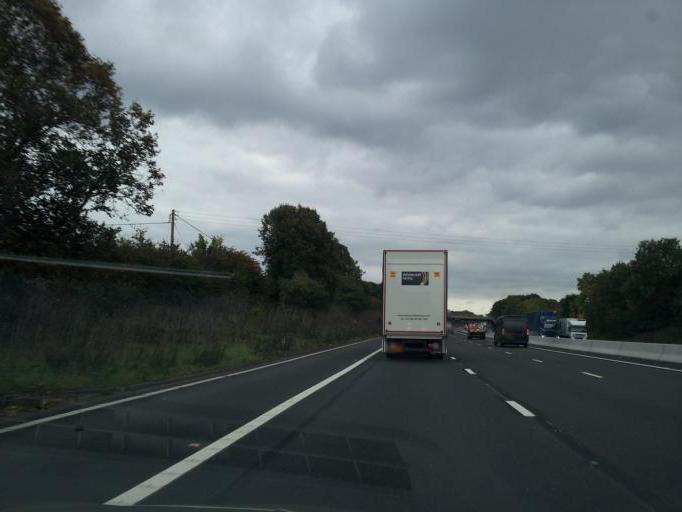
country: GB
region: England
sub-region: Northamptonshire
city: Blisworth
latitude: 52.2056
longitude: -0.9298
